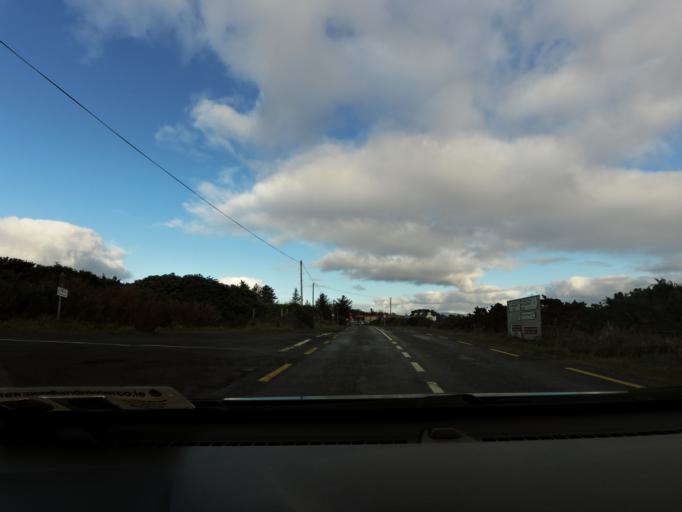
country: IE
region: Connaught
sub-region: Maigh Eo
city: Belmullet
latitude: 53.9508
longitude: -9.9743
